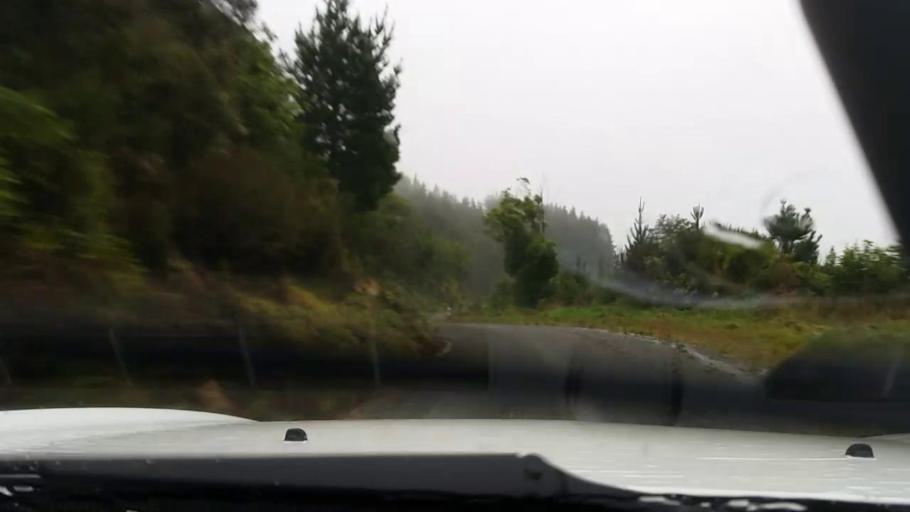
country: NZ
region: Wellington
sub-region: Masterton District
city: Masterton
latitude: -41.1907
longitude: 175.8159
